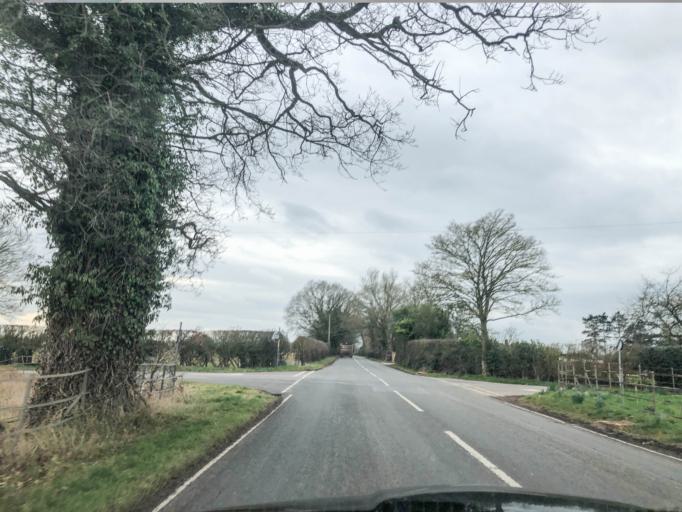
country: GB
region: England
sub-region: Warwickshire
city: Wroxall
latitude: 52.3120
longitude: -1.6773
